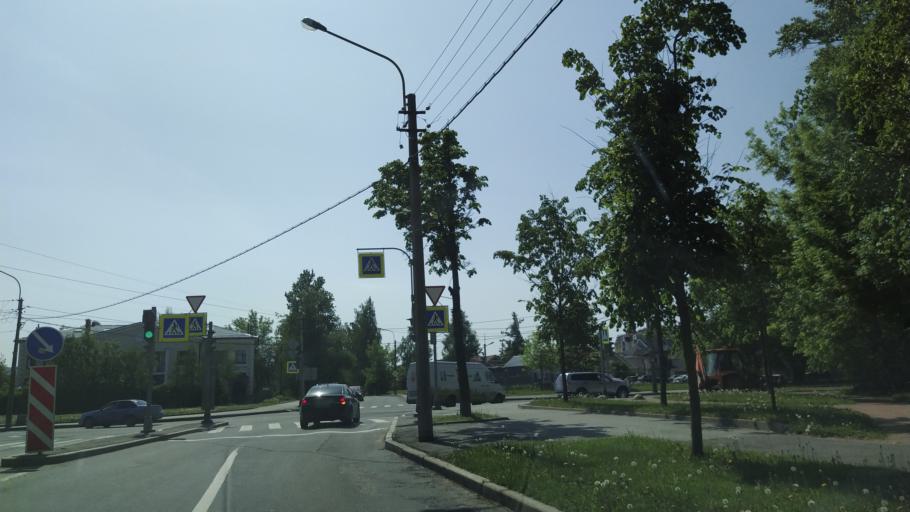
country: RU
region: St.-Petersburg
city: Pushkin
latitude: 59.7033
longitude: 30.4072
